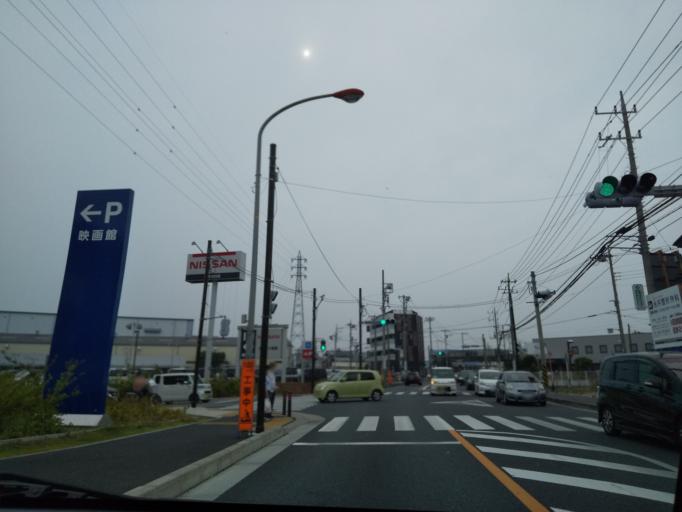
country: JP
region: Kanagawa
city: Minami-rinkan
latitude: 35.5022
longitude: 139.4255
